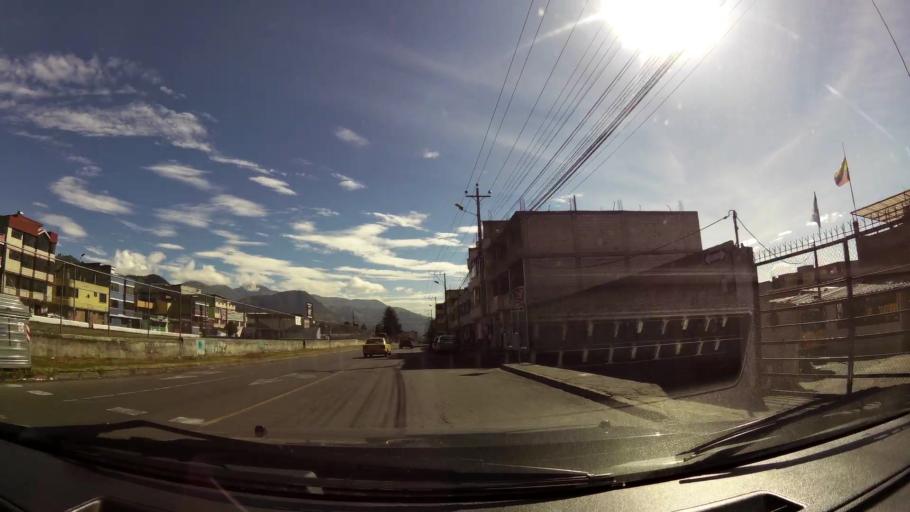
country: EC
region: Pichincha
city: Quito
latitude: -0.2931
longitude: -78.5624
